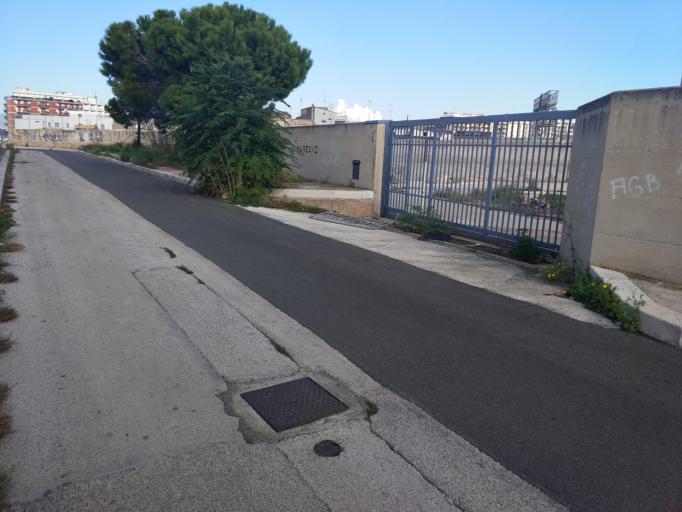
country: IT
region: Apulia
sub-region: Provincia di Bari
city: Bari
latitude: 41.1151
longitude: 16.8528
